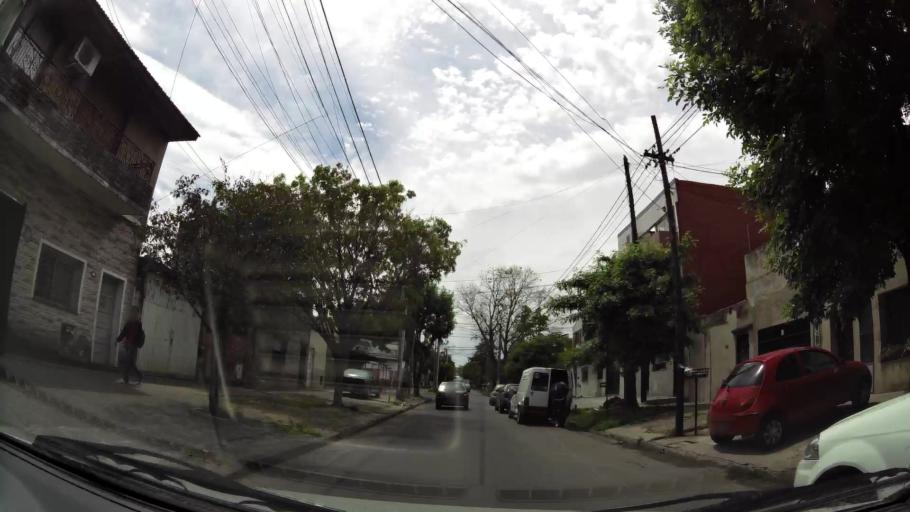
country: AR
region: Buenos Aires
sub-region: Partido de Avellaneda
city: Avellaneda
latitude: -34.6780
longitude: -58.3718
